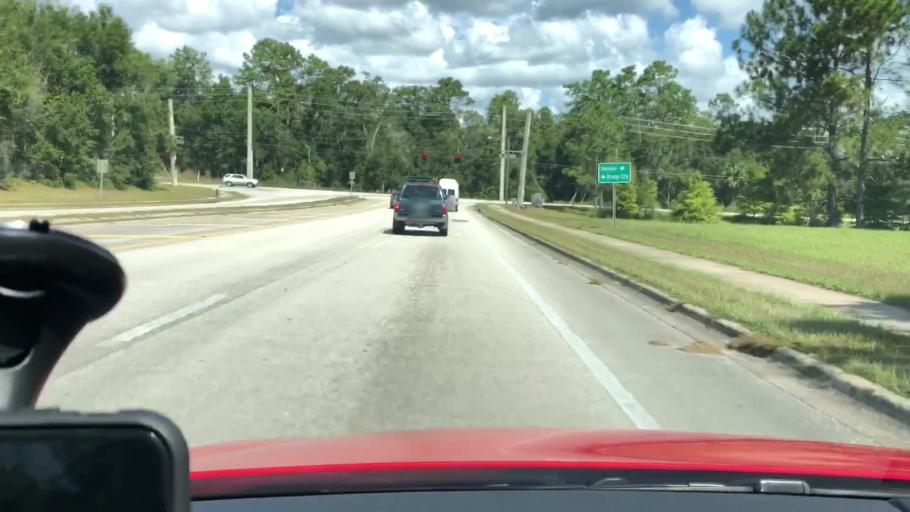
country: US
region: Florida
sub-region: Volusia County
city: Orange City
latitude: 28.9477
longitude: -81.2710
